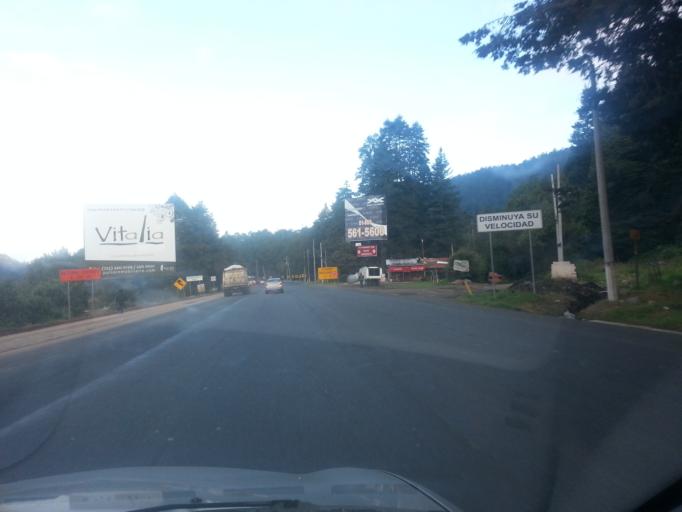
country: MX
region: Morelos
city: San Jeronimo Acazulco
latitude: 19.2990
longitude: -99.4002
